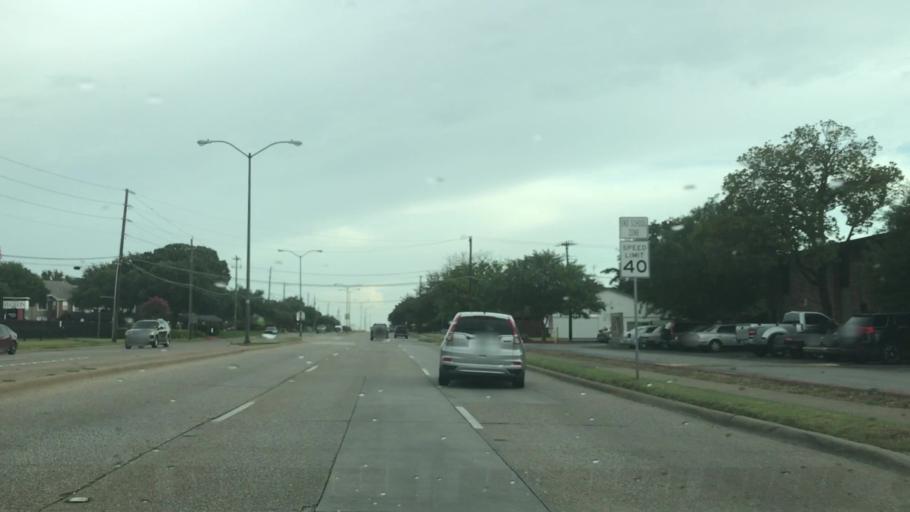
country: US
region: Texas
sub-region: Dallas County
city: Garland
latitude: 32.8706
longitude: -96.6832
